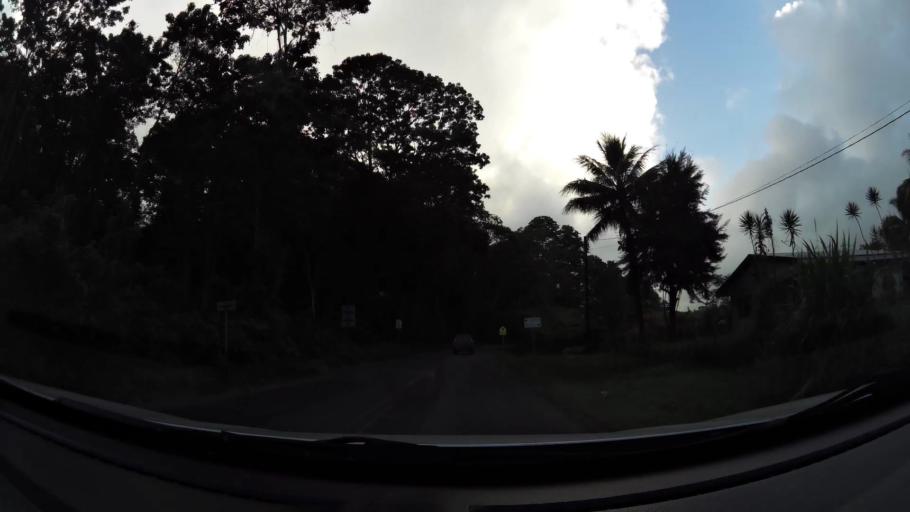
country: CR
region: Cartago
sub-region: Canton de Turrialba
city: La Suiza
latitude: 9.9604
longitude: -83.5692
